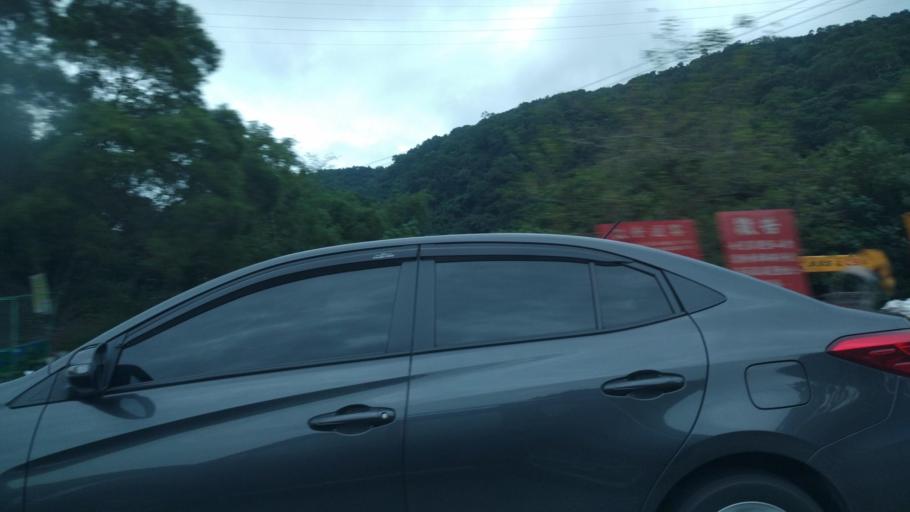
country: TW
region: Taiwan
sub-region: Yilan
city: Yilan
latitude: 24.6024
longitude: 121.8376
